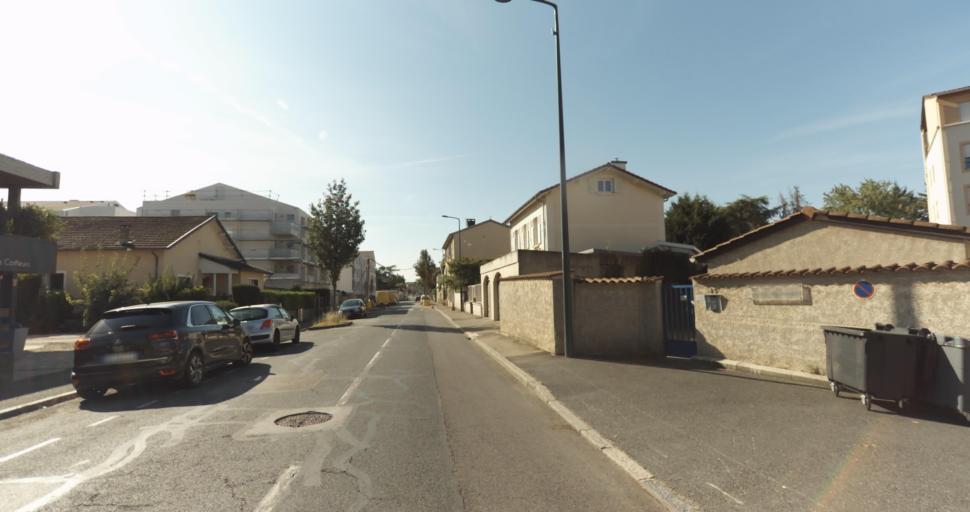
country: FR
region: Rhone-Alpes
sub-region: Departement du Rhone
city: Neuville-sur-Saone
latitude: 45.8809
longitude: 4.8375
